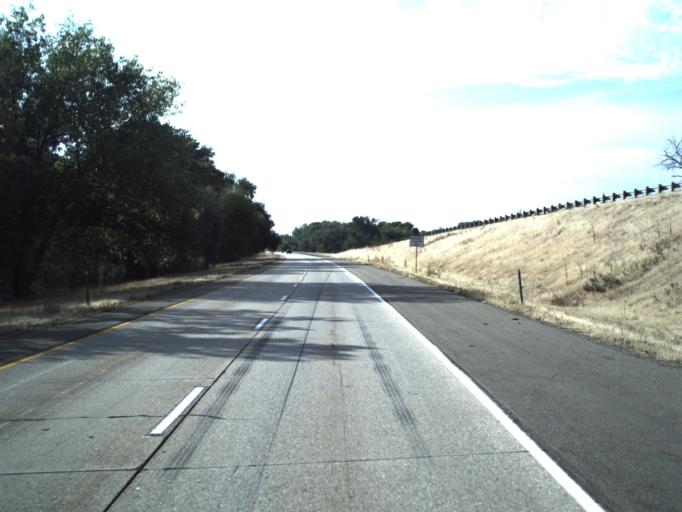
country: US
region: Utah
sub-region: Weber County
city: Washington Terrace
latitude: 41.1507
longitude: -111.9691
